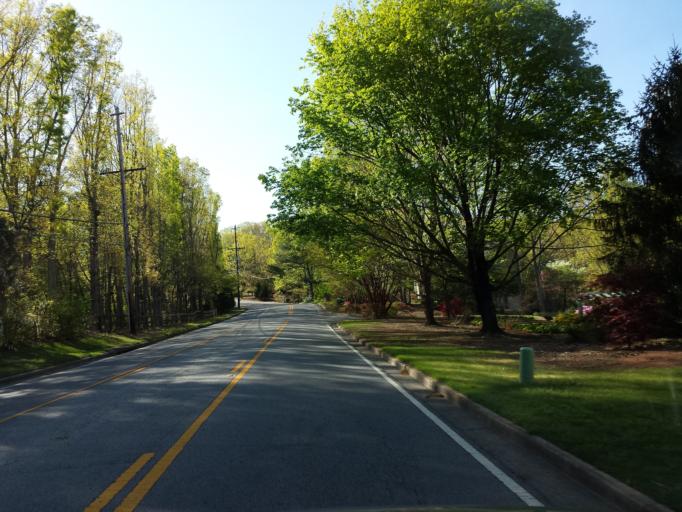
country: US
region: Georgia
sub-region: Cobb County
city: Marietta
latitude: 33.9758
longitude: -84.4944
